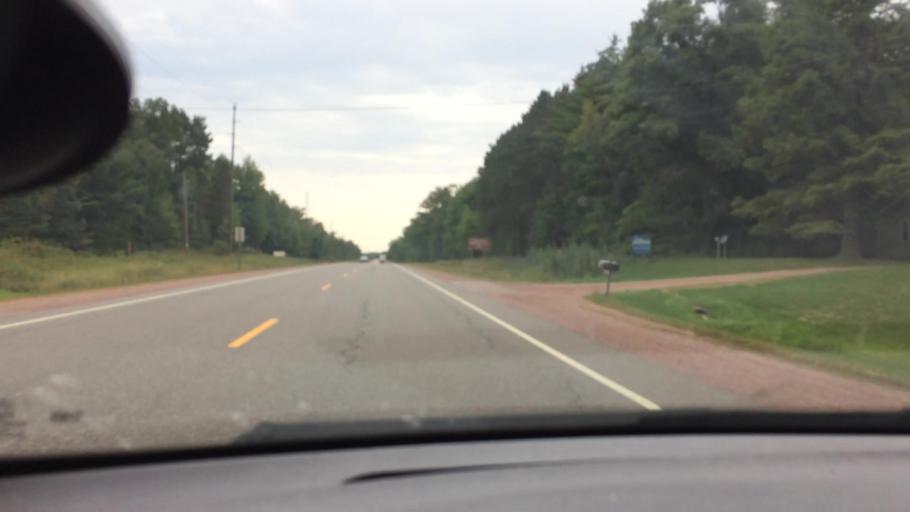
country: US
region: Wisconsin
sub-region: Clark County
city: Neillsville
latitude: 44.5744
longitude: -90.7325
